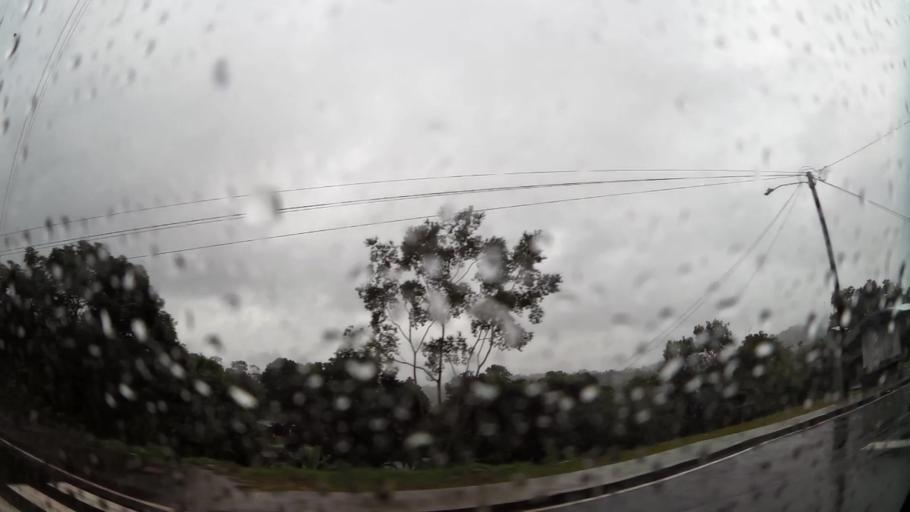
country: PA
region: Colon
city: Quebrada Bonita Adentro
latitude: 9.2859
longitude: -79.7266
